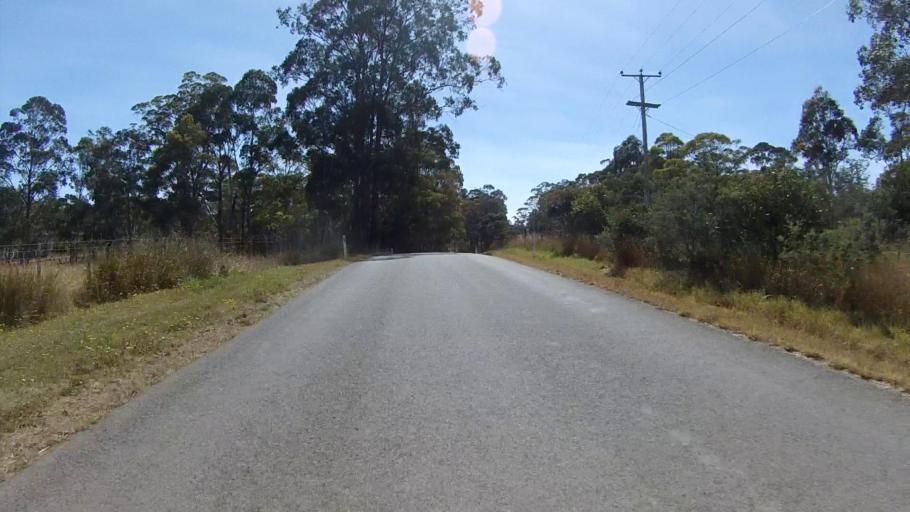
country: AU
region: Tasmania
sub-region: Sorell
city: Sorell
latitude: -42.7525
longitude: 147.7099
